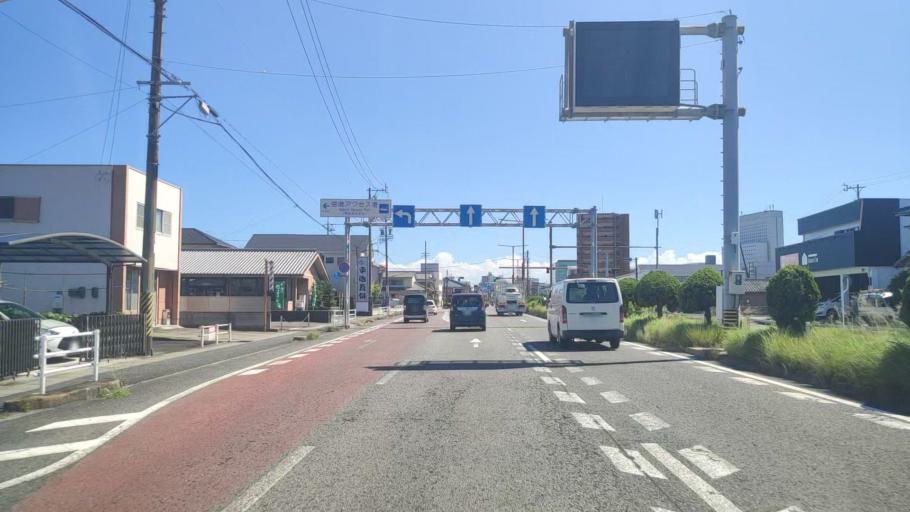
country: JP
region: Mie
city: Tsu-shi
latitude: 34.7397
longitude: 136.5154
